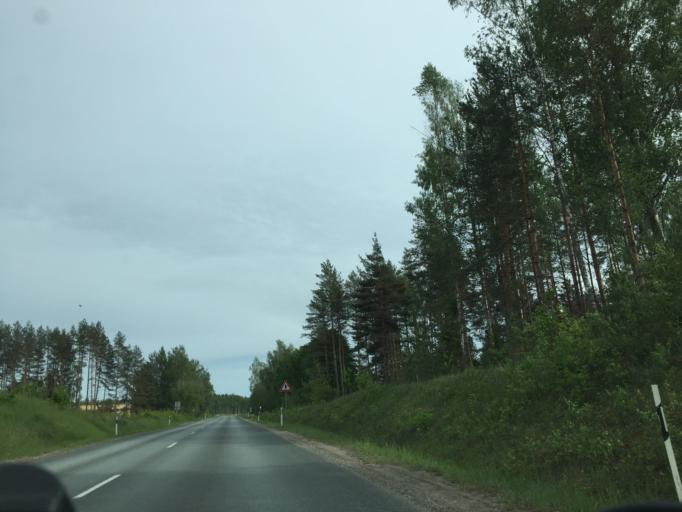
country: LV
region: Valmieras Rajons
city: Valmiera
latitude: 57.4683
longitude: 25.4083
